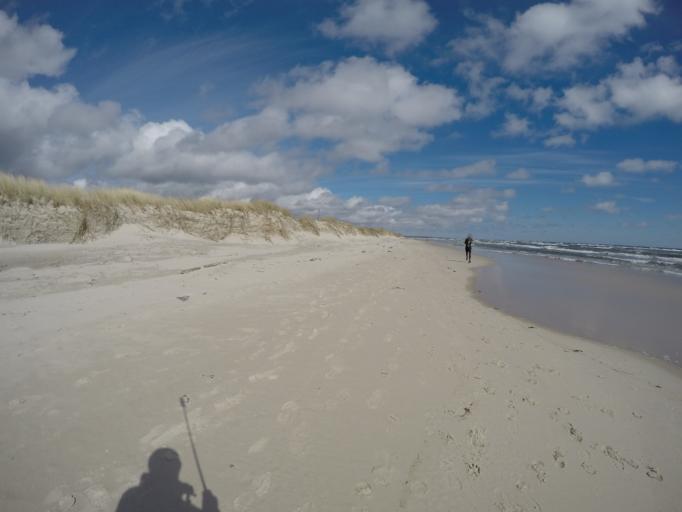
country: SE
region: Skane
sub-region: Simrishamns Kommun
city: Simrishamn
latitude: 55.3940
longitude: 14.2097
